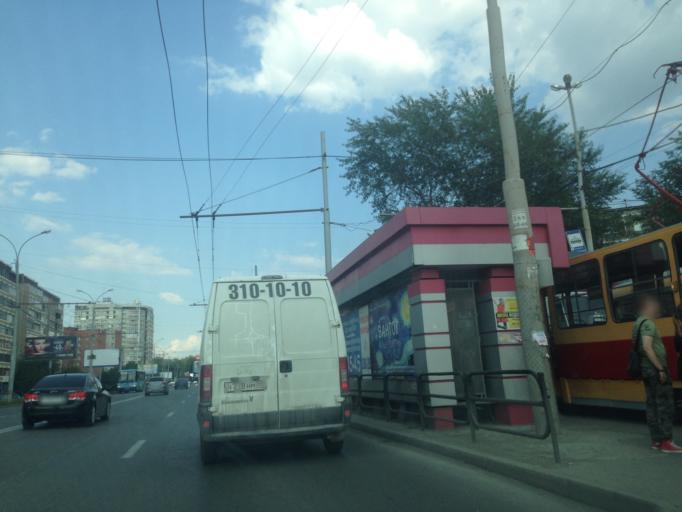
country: RU
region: Sverdlovsk
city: Yekaterinburg
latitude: 56.8591
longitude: 60.6205
